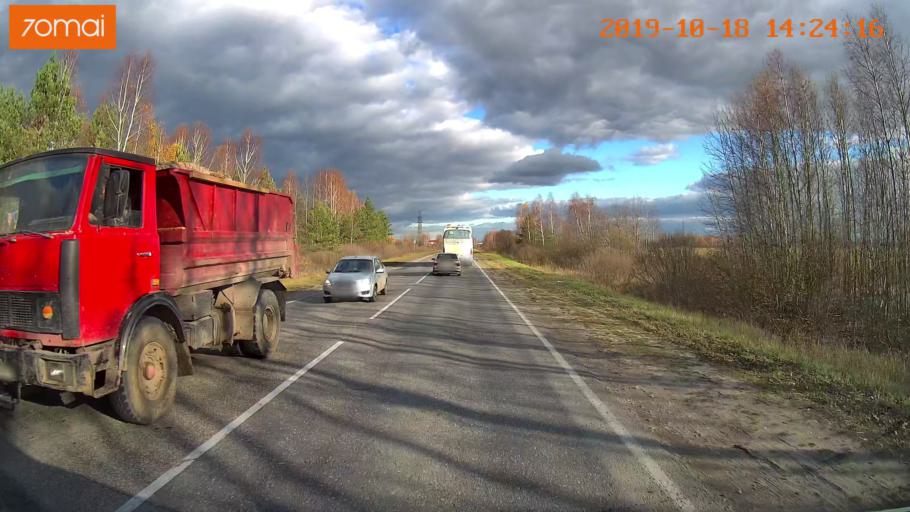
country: RU
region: Rjazan
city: Tuma
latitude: 55.1474
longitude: 40.4968
